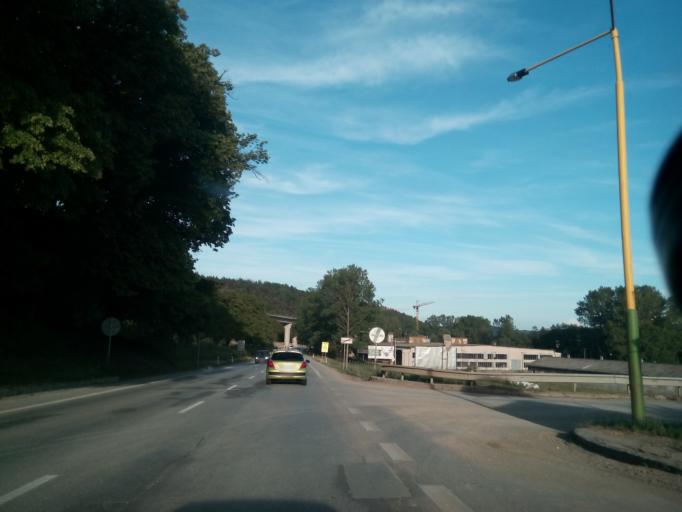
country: SK
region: Presovsky
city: Sabinov
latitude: 49.0207
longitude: 21.0307
